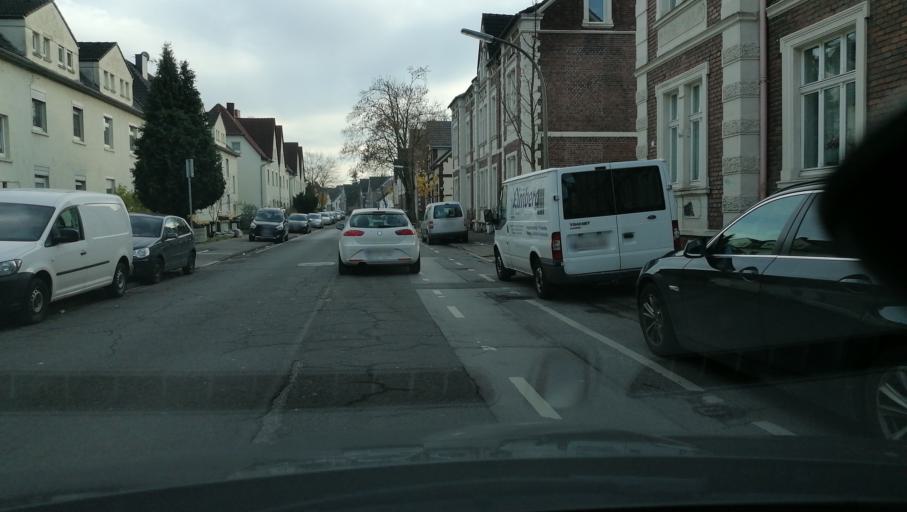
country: DE
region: North Rhine-Westphalia
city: Waltrop
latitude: 51.5676
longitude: 7.3745
